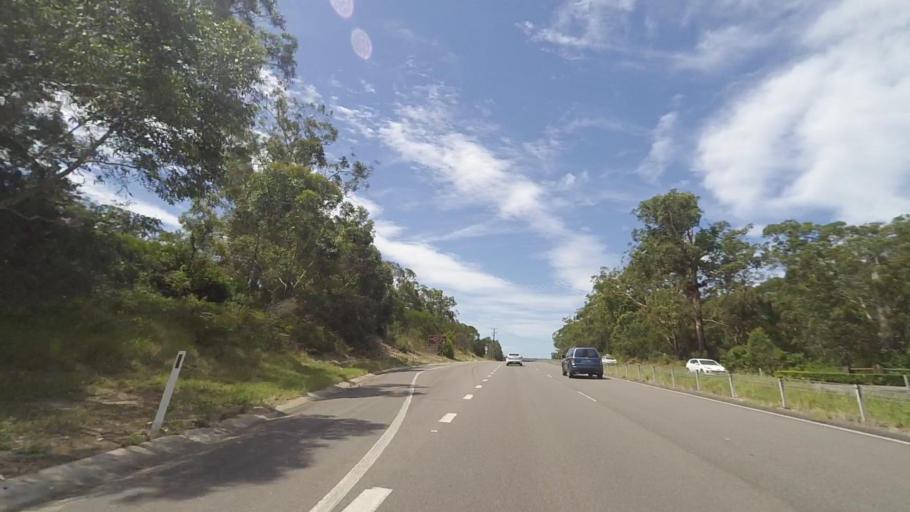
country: AU
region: New South Wales
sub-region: Port Stephens Shire
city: Anna Bay
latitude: -32.7708
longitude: 152.0115
